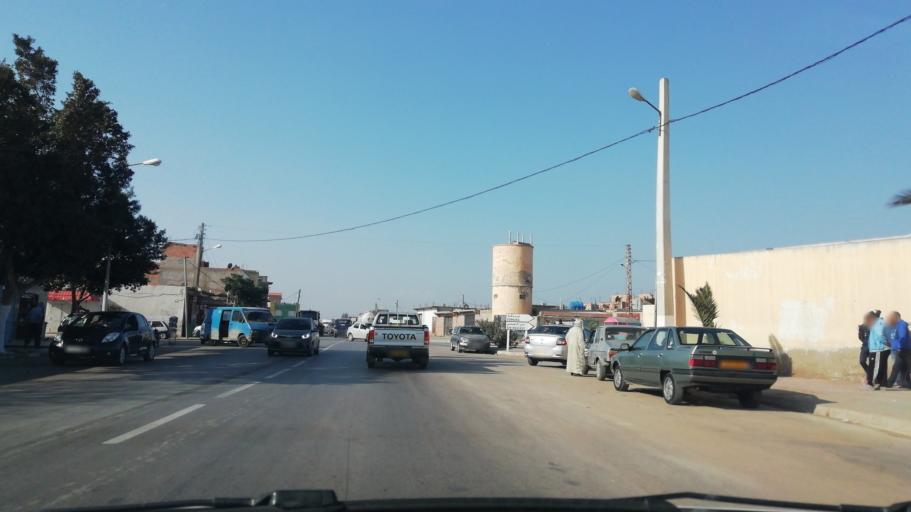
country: DZ
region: Mostaganem
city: Mostaganem
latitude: 35.7408
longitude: -0.0262
